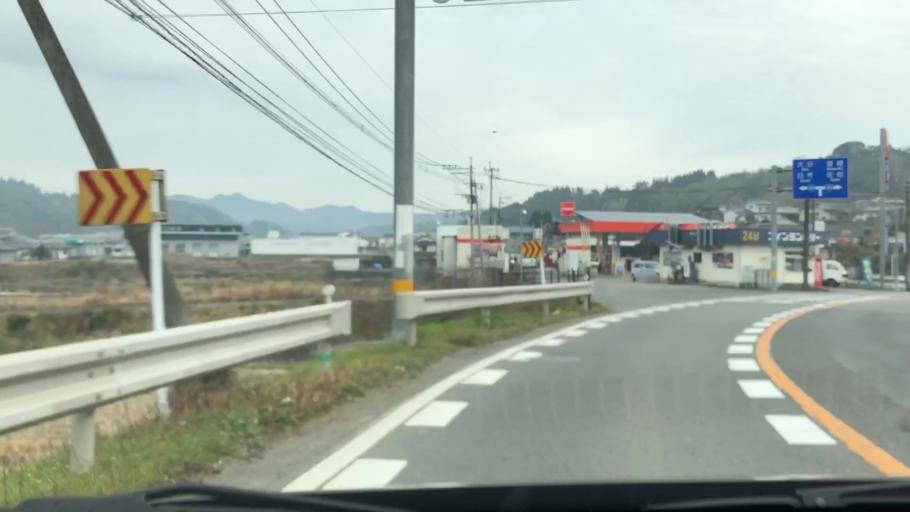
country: JP
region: Oita
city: Usuki
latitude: 33.0324
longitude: 131.6886
